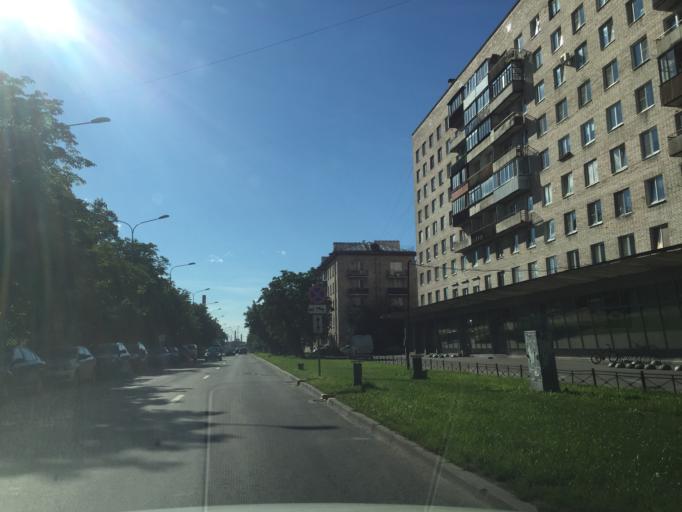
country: RU
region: St.-Petersburg
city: Avtovo
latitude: 59.8716
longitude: 30.3094
